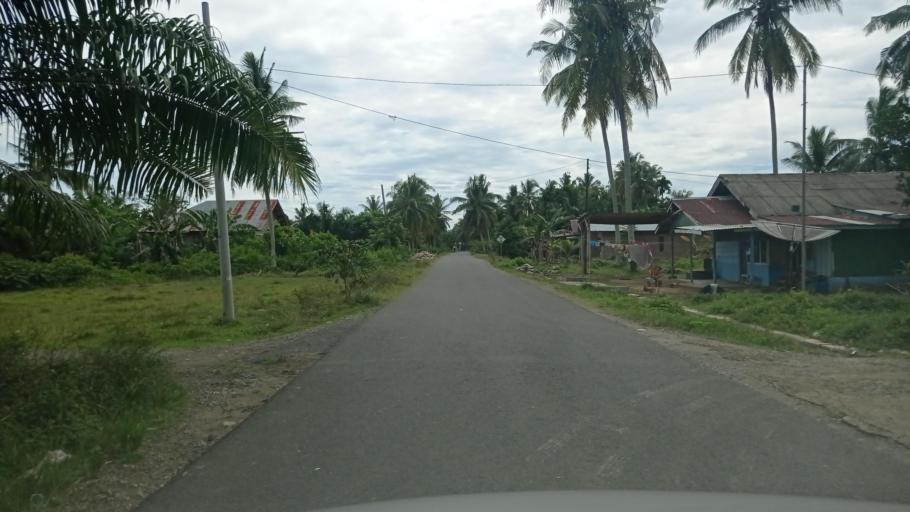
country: ID
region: Bengkulu
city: Ipuh
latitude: -2.5683
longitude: 101.1103
